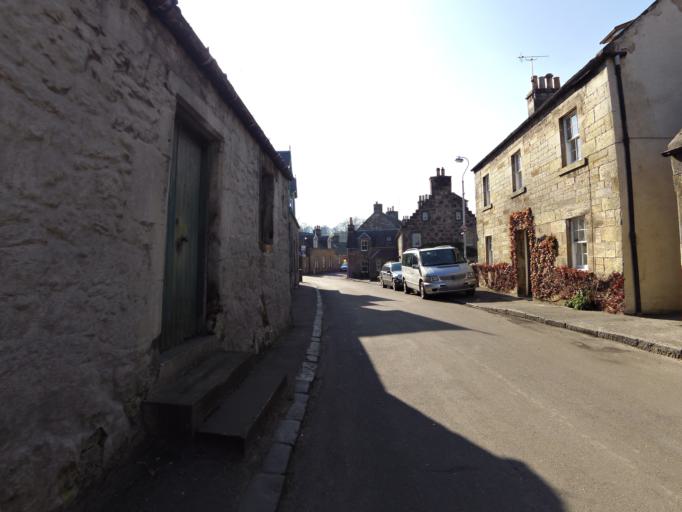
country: GB
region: Scotland
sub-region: Fife
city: Falkland
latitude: 56.2529
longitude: -3.2111
